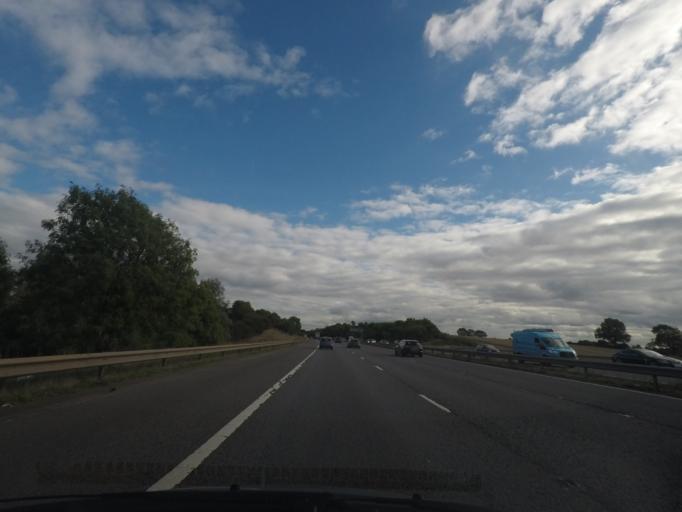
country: GB
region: England
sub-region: Leicestershire
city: Markfield
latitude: 52.6762
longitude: -1.2860
